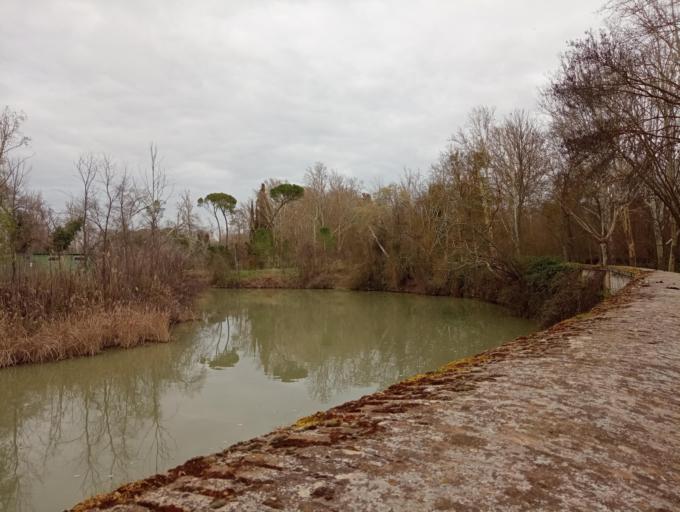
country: ES
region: Madrid
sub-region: Provincia de Madrid
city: Aranjuez
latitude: 40.0403
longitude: -3.5973
